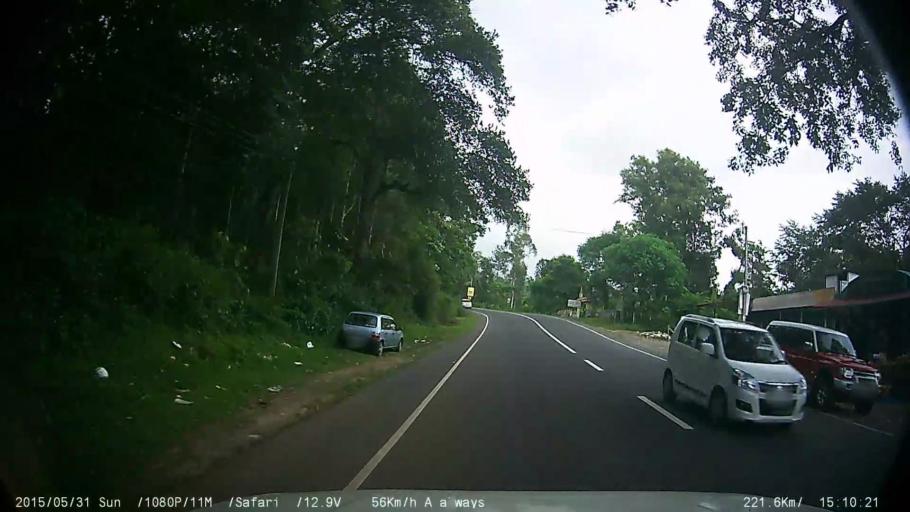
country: IN
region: Kerala
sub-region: Wayanad
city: Panamaram
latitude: 11.6559
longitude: 76.2253
